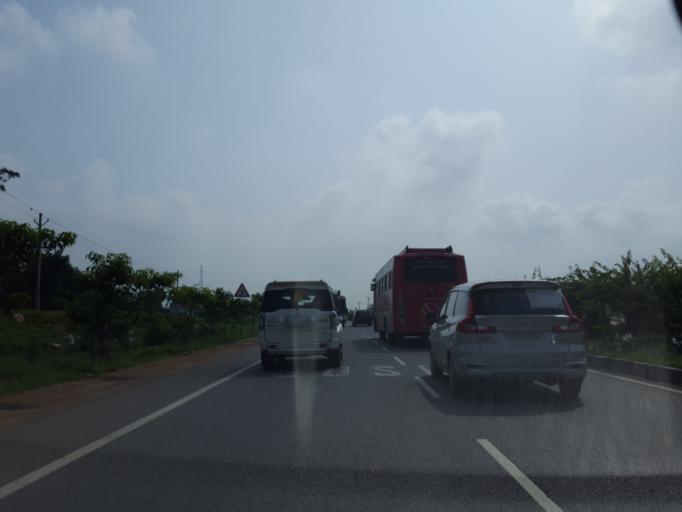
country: IN
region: Telangana
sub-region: Rangareddi
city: Ghatkesar
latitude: 17.2795
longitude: 78.7883
